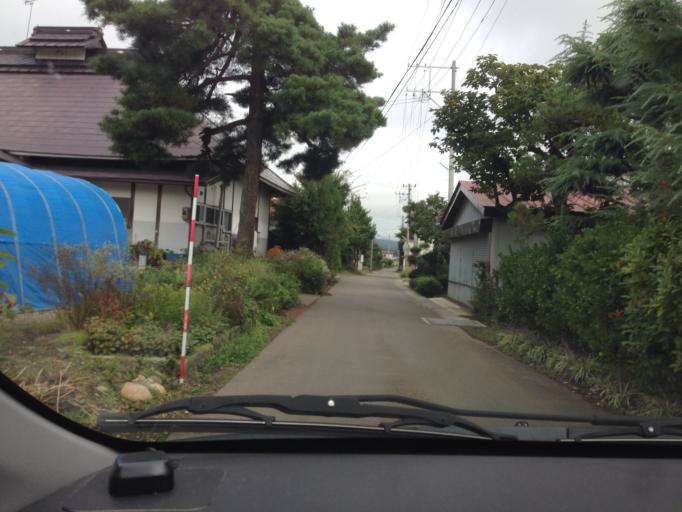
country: JP
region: Fukushima
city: Kitakata
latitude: 37.5480
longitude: 139.8027
